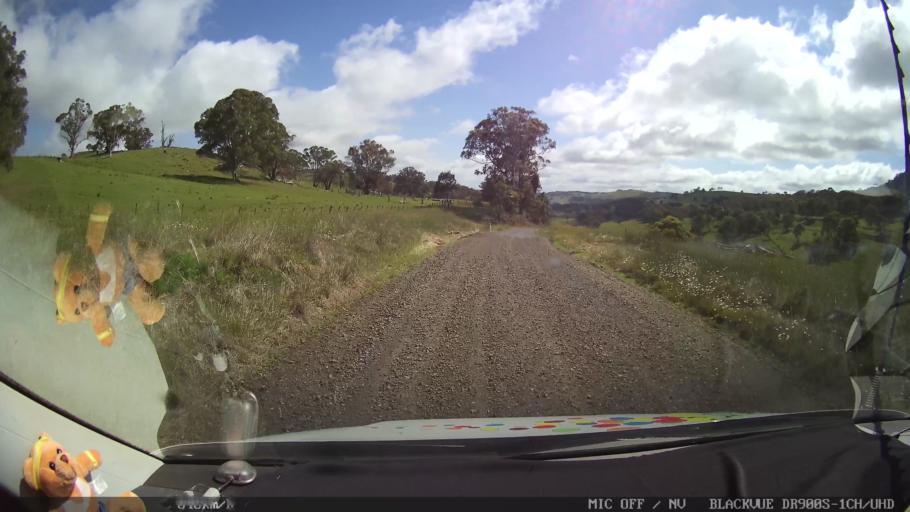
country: AU
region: New South Wales
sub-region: Guyra
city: Guyra
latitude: -30.0027
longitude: 151.6698
